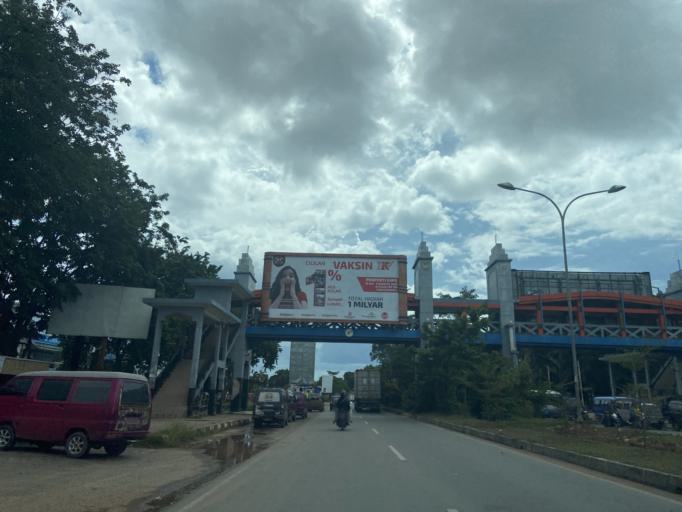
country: SG
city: Singapore
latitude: 1.0419
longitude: 103.9831
